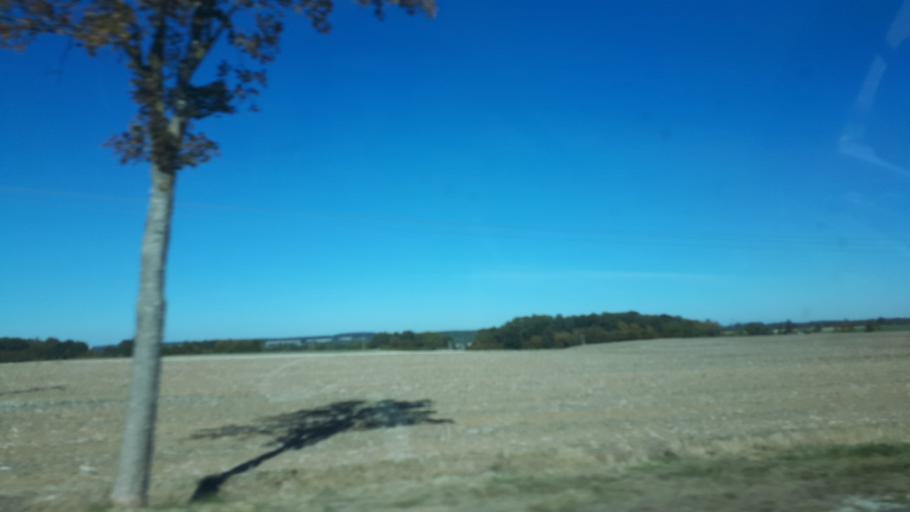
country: FR
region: Centre
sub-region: Departement d'Eure-et-Loir
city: La Chapelle-du-Noyer
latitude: 48.0503
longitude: 1.3202
